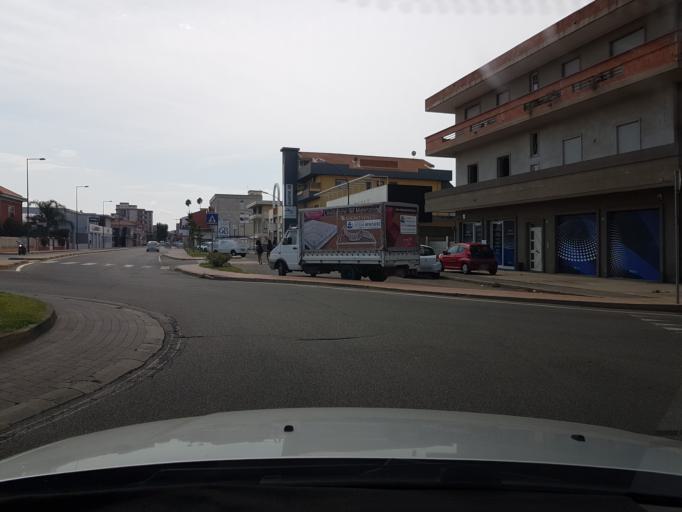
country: IT
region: Sardinia
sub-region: Provincia di Oristano
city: Oristano
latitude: 39.9121
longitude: 8.5872
